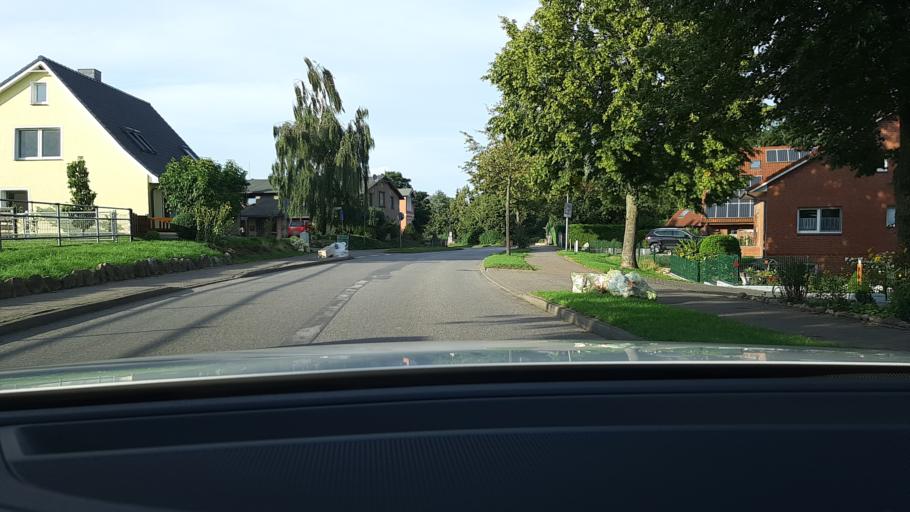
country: DE
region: Schleswig-Holstein
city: Heilshoop
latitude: 53.8848
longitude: 10.5298
